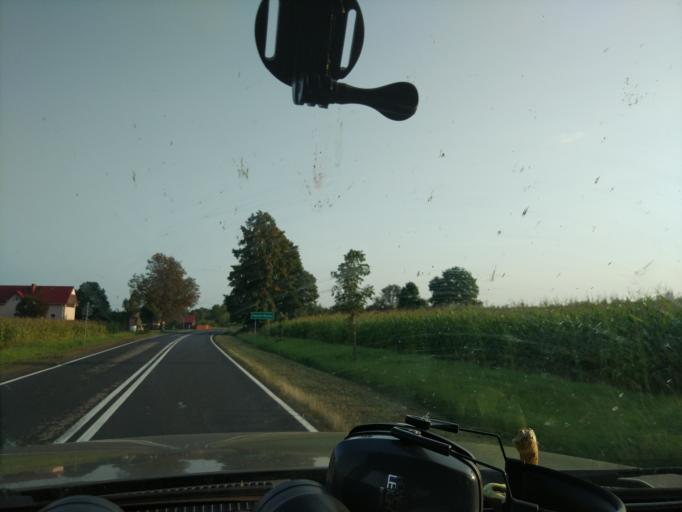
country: PL
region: Warmian-Masurian Voivodeship
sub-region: Powiat szczycienski
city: Wielbark
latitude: 53.3504
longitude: 20.9004
